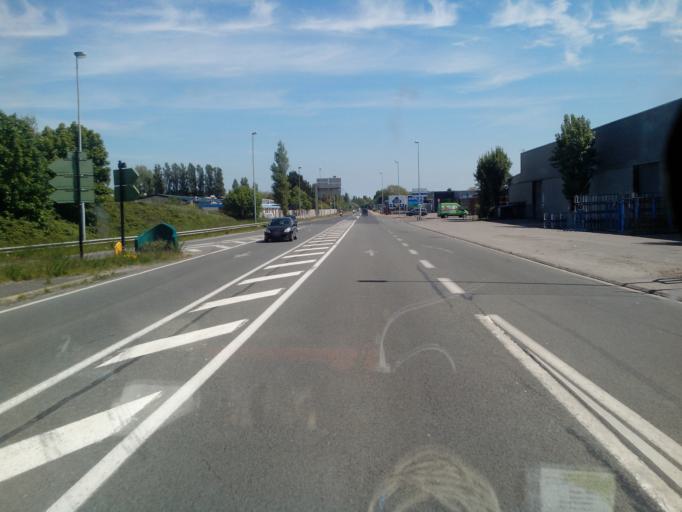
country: FR
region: Nord-Pas-de-Calais
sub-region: Departement du Pas-de-Calais
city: Saint-Leonard
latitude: 50.6928
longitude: 1.6114
